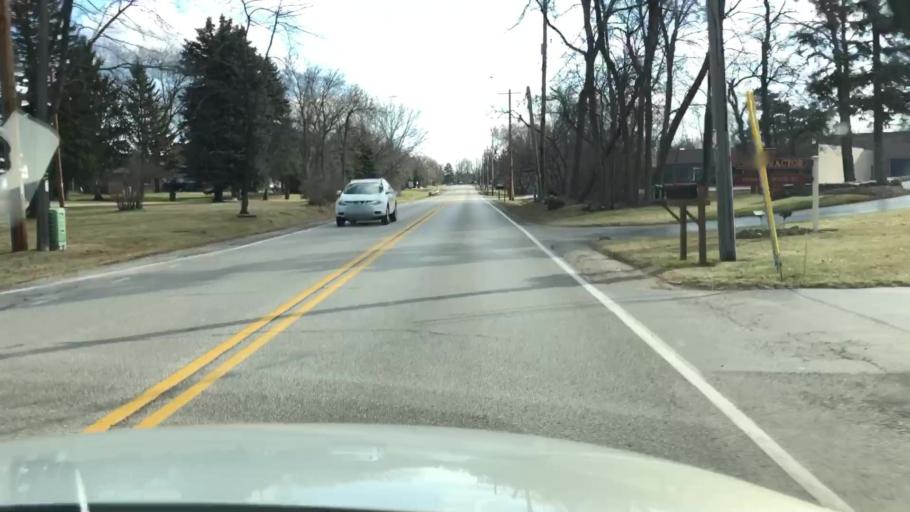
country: US
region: Wisconsin
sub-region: Waukesha County
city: Waukesha
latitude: 43.0427
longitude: -88.1767
